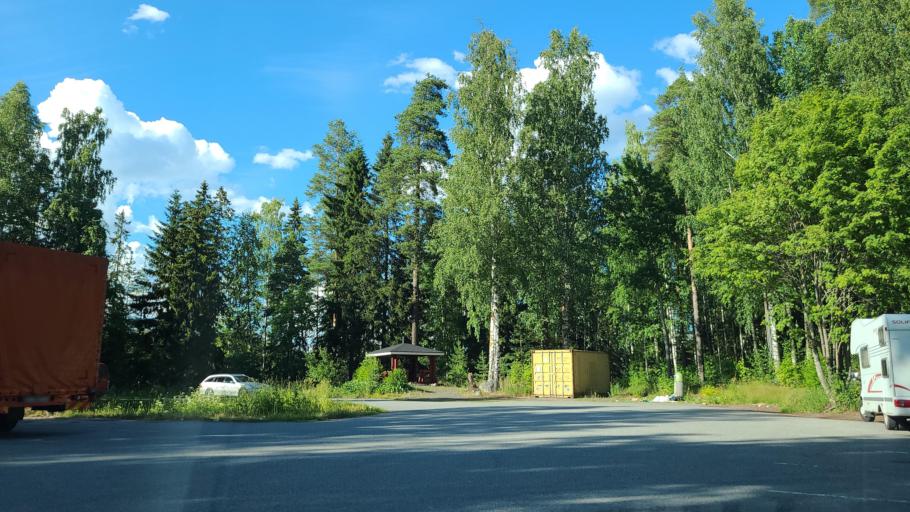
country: FI
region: Pirkanmaa
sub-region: Tampere
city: Kangasala
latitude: 61.5440
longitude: 24.0411
